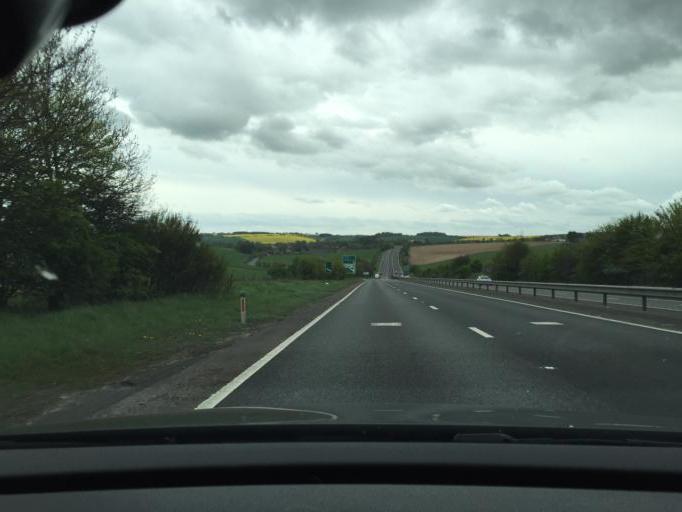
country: GB
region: England
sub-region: Oxfordshire
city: Harwell
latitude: 51.5399
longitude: -1.2937
